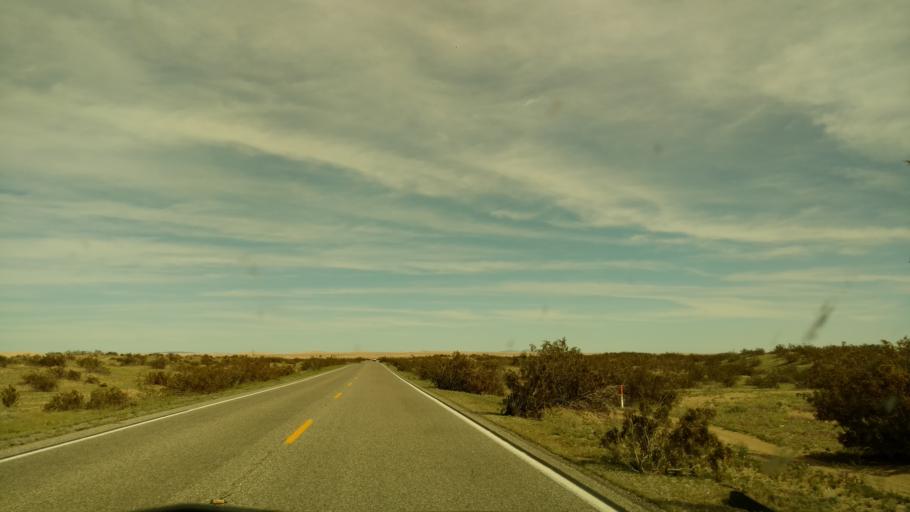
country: US
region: California
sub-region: Imperial County
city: Holtville
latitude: 32.9705
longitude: -115.2278
